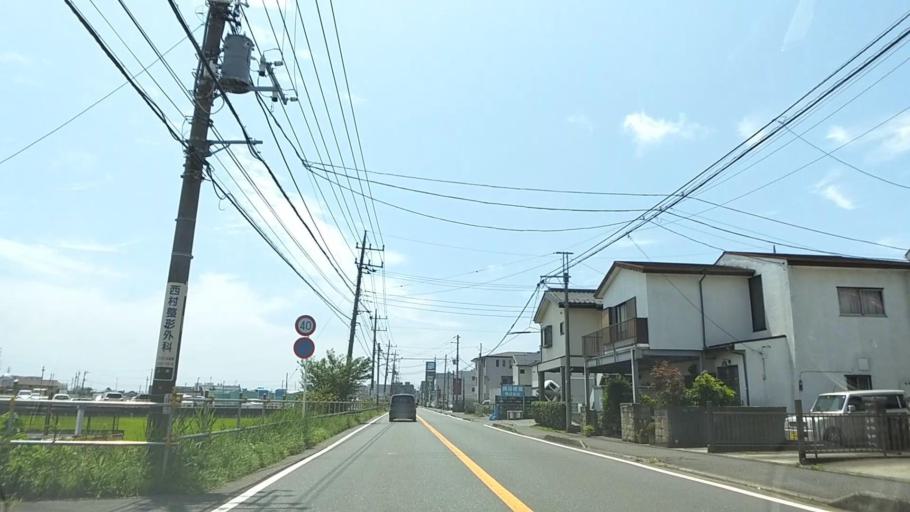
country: JP
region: Kanagawa
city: Zama
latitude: 35.4584
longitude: 139.3856
